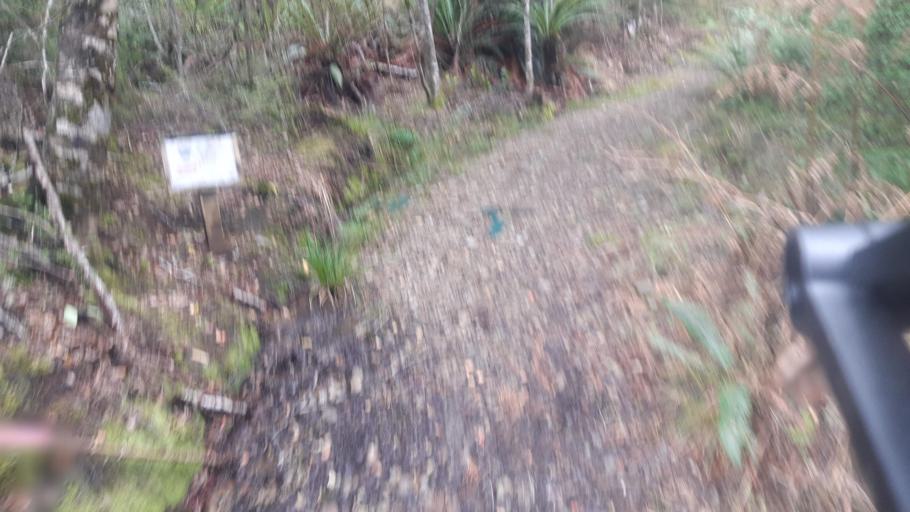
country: NZ
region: Tasman
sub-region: Tasman District
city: Wakefield
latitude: -41.7610
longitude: 172.8039
